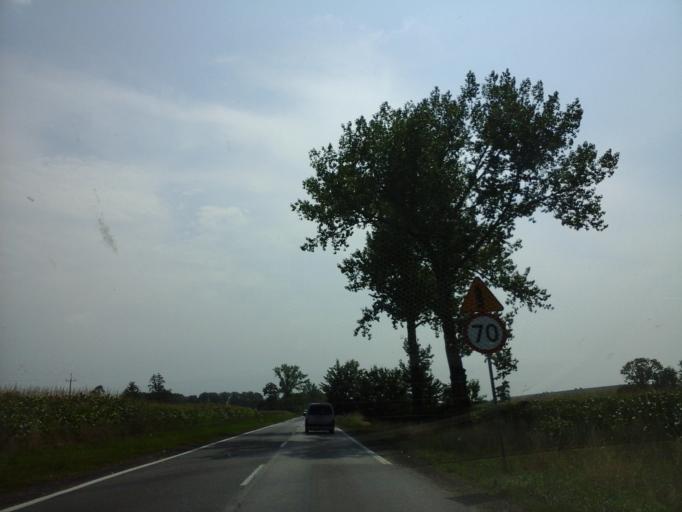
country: PL
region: Lower Silesian Voivodeship
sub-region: Powiat wroclawski
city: Zorawina
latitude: 50.9768
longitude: 17.0707
